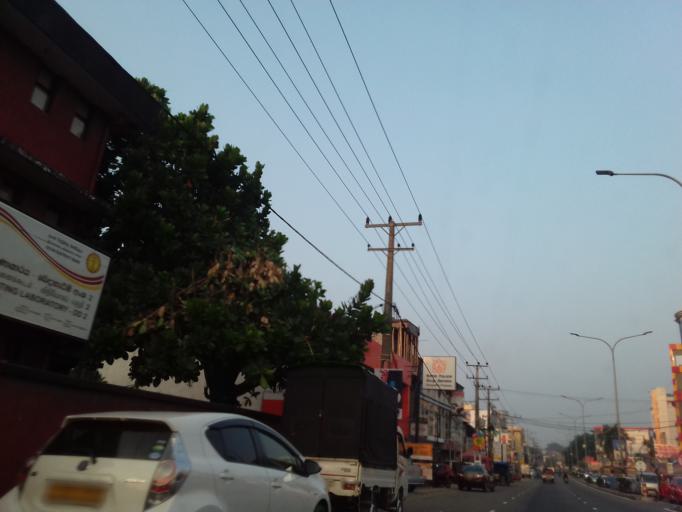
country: LK
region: Western
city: Kelaniya
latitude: 6.9826
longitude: 79.9314
